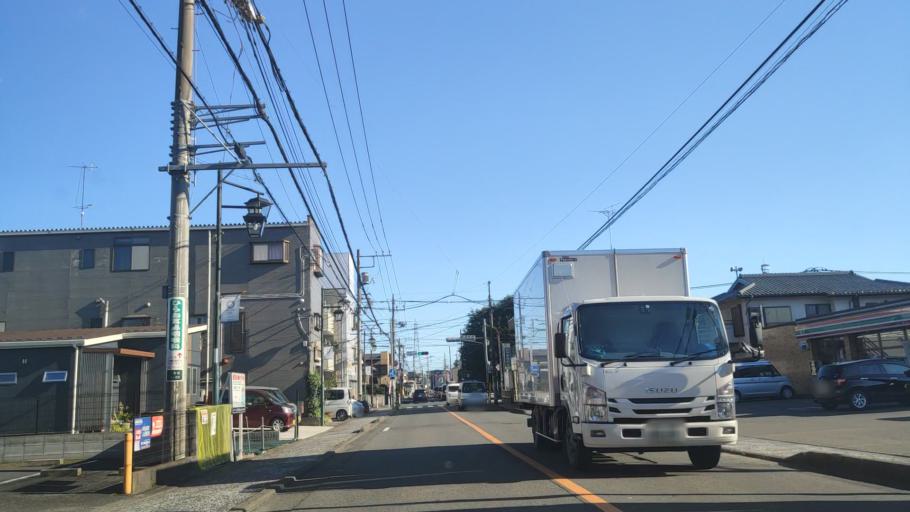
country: JP
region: Tokyo
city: Hachioji
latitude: 35.5948
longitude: 139.3211
